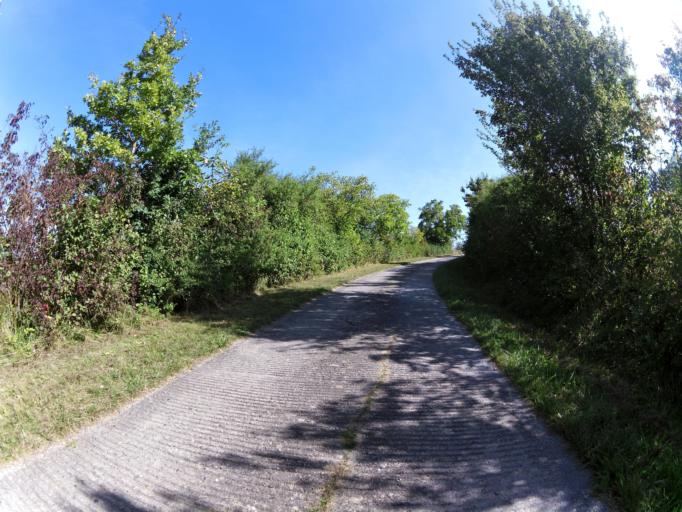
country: DE
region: Bavaria
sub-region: Regierungsbezirk Unterfranken
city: Guntersleben
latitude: 49.8597
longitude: 9.9011
